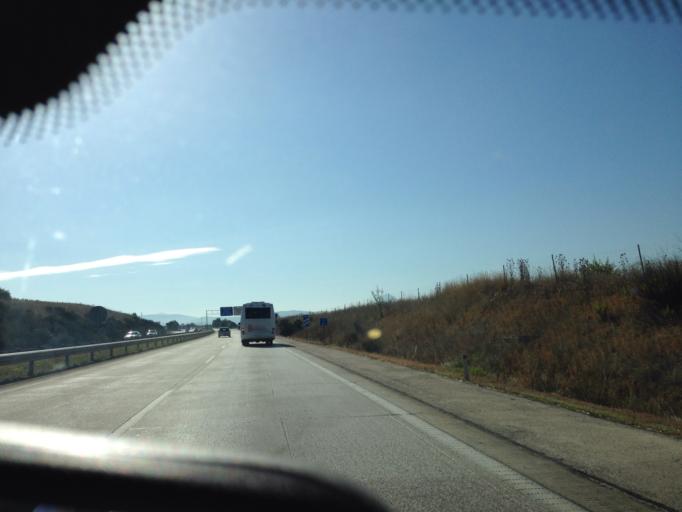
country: ES
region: Navarre
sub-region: Provincia de Navarra
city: Iturrama
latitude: 42.7883
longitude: -1.6608
